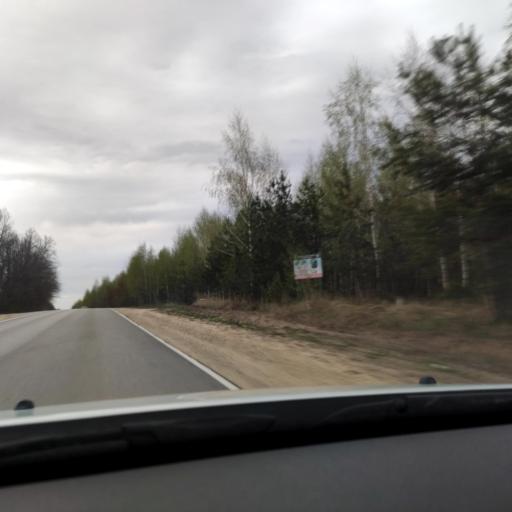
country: RU
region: Lipetsk
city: Zadonsk
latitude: 52.4250
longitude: 38.9523
